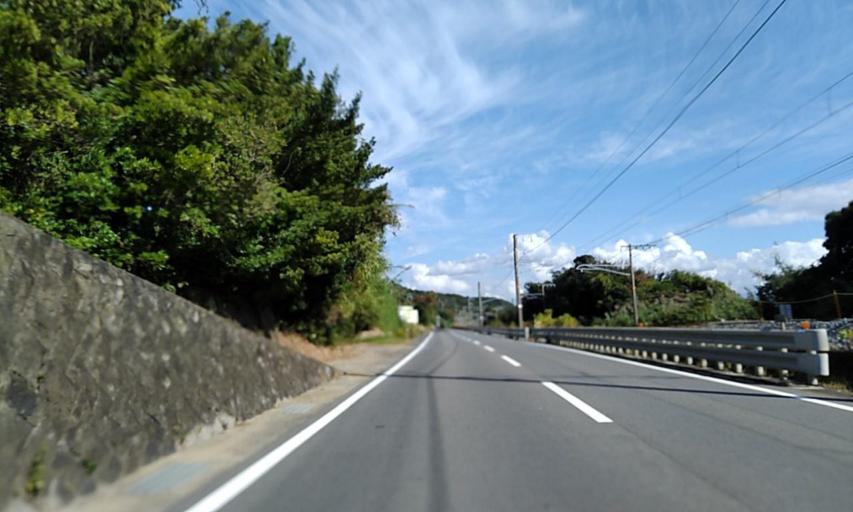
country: JP
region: Wakayama
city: Tanabe
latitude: 33.7826
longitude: 135.2504
